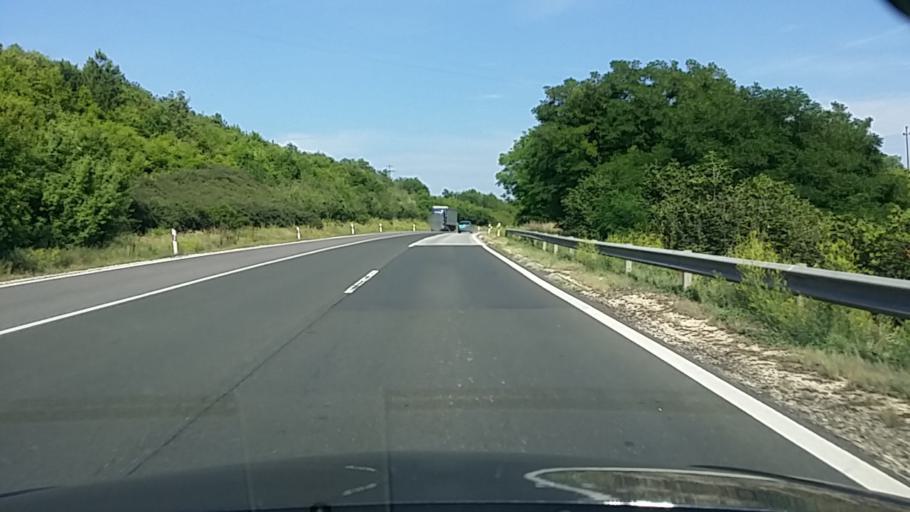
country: HU
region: Pest
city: Vac
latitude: 47.7998
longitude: 19.1430
